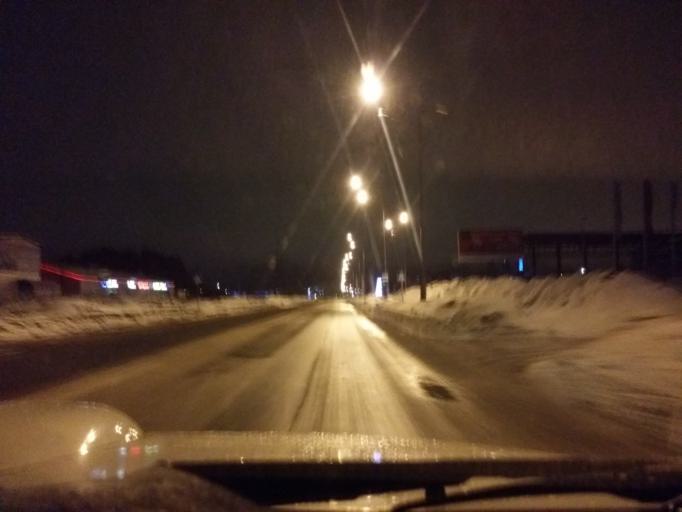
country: RU
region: Khanty-Mansiyskiy Avtonomnyy Okrug
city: Nizhnevartovsk
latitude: 60.9639
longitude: 76.5505
